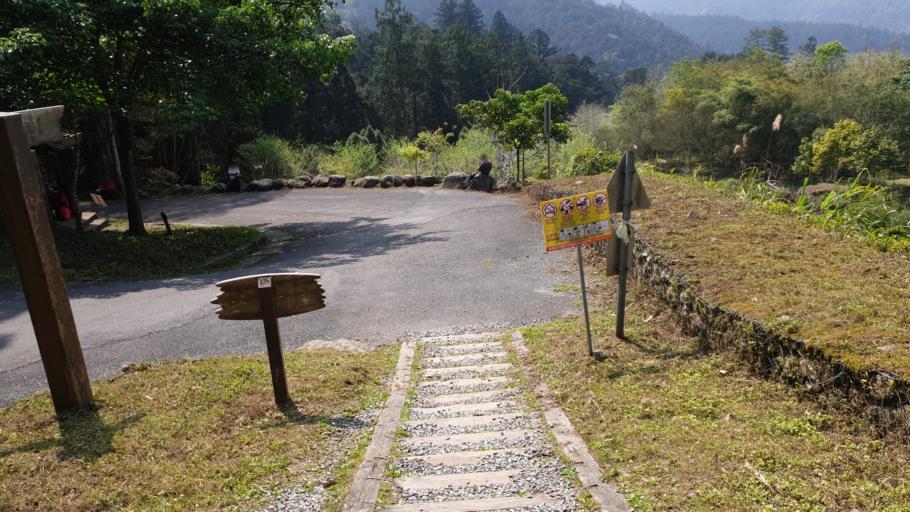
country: TW
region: Taiwan
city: Lugu
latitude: 23.6732
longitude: 120.8005
